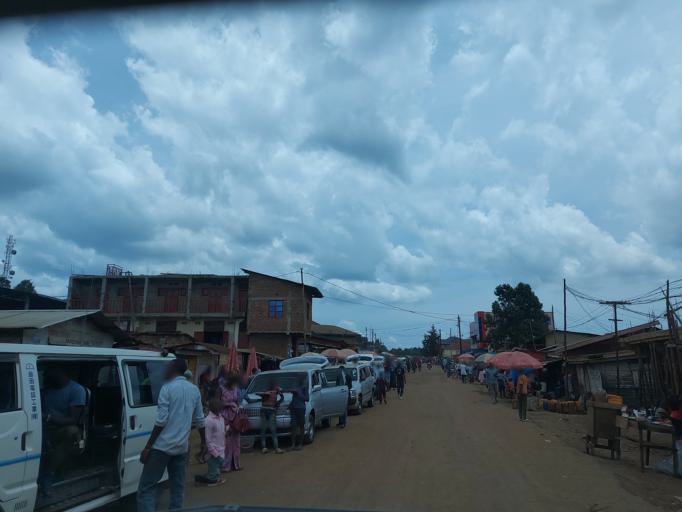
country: CD
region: South Kivu
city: Bukavu
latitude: -2.2968
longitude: 28.7988
